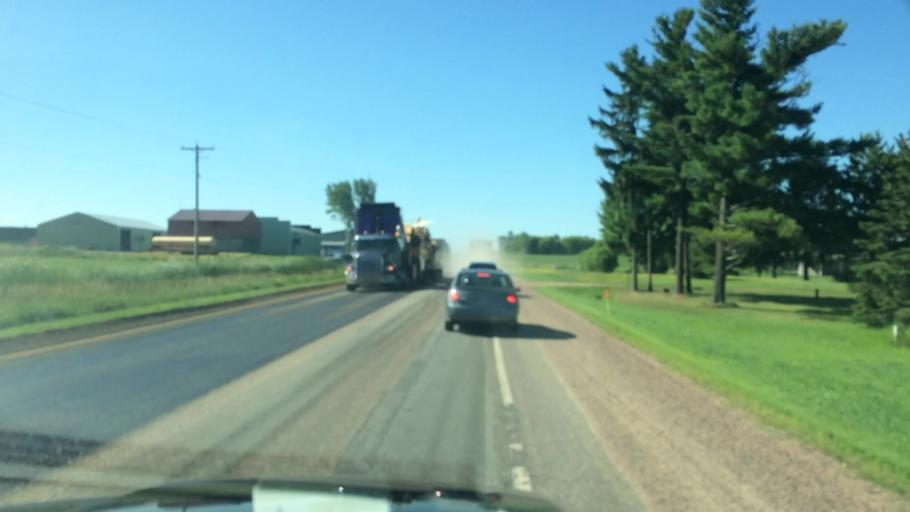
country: US
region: Wisconsin
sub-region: Marathon County
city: Stratford
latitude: 44.8943
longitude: -90.0788
